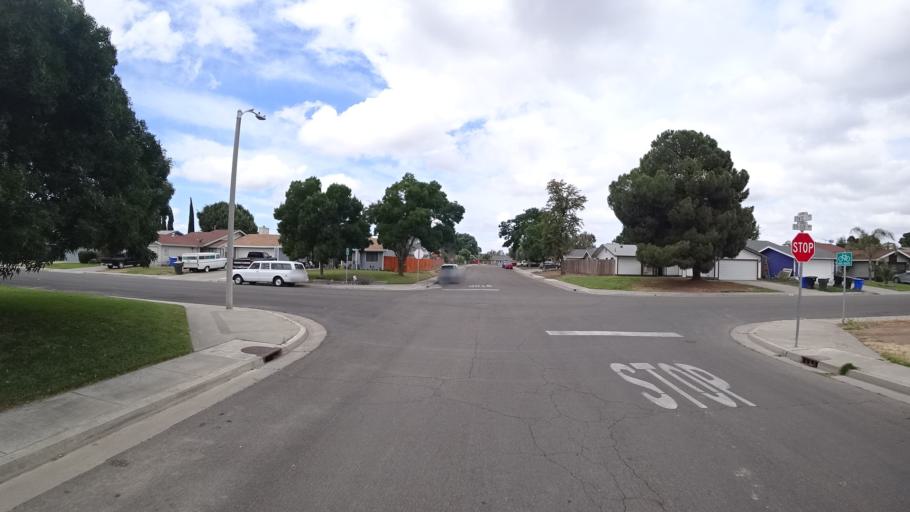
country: US
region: California
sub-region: Kings County
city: Hanford
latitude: 36.3114
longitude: -119.6633
